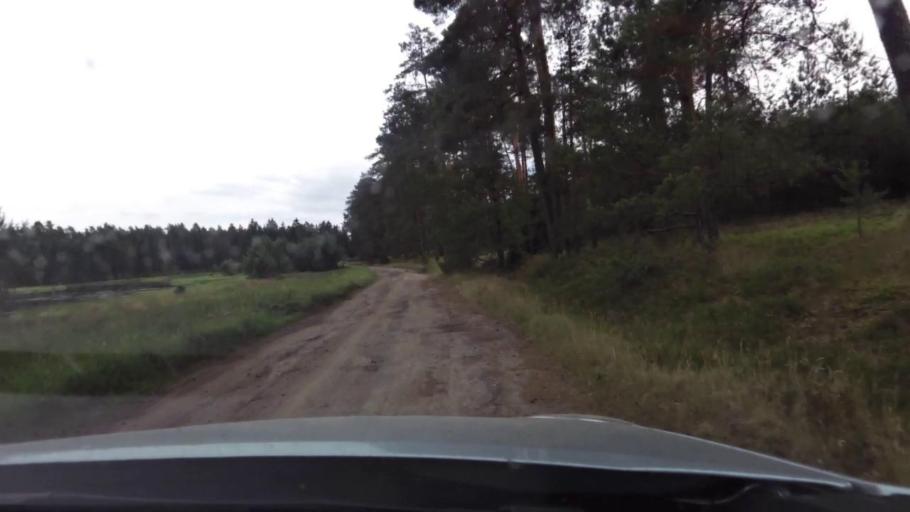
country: PL
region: Pomeranian Voivodeship
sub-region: Powiat bytowski
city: Trzebielino
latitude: 54.1990
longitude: 17.0079
